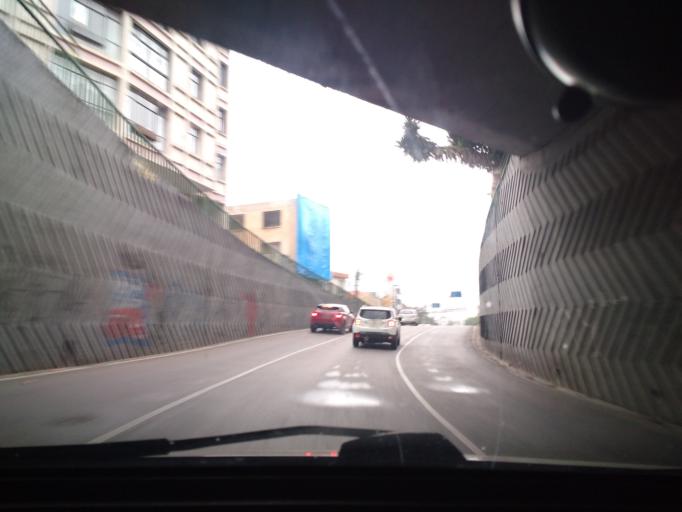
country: BR
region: Parana
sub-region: Curitiba
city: Curitiba
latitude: -25.4261
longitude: -49.2789
